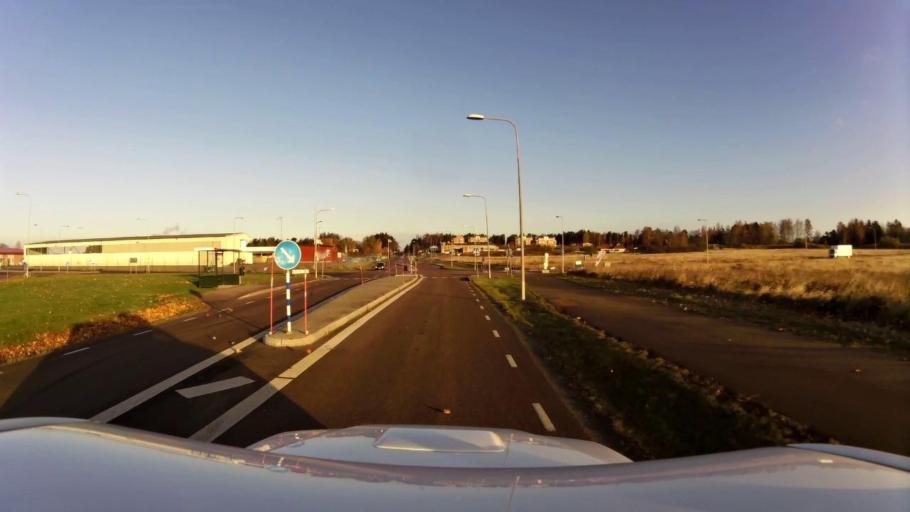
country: SE
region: OEstergoetland
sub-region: Linkopings Kommun
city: Linkoping
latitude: 58.4228
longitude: 15.6790
